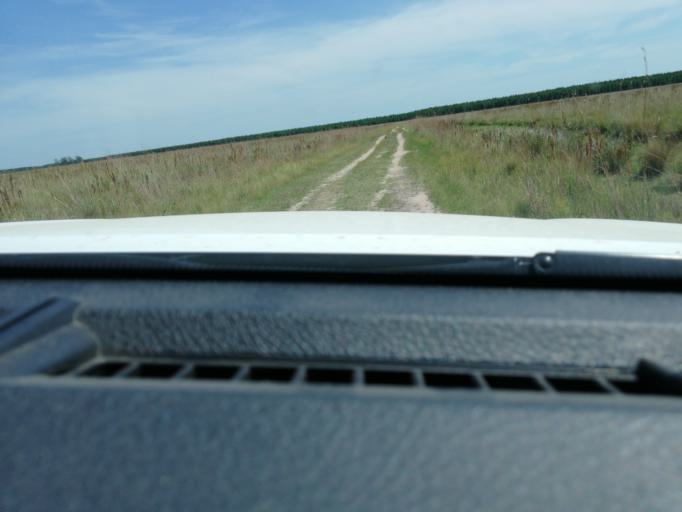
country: AR
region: Corrientes
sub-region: Departamento de San Miguel
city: San Miguel
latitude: -28.0477
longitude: -57.4555
